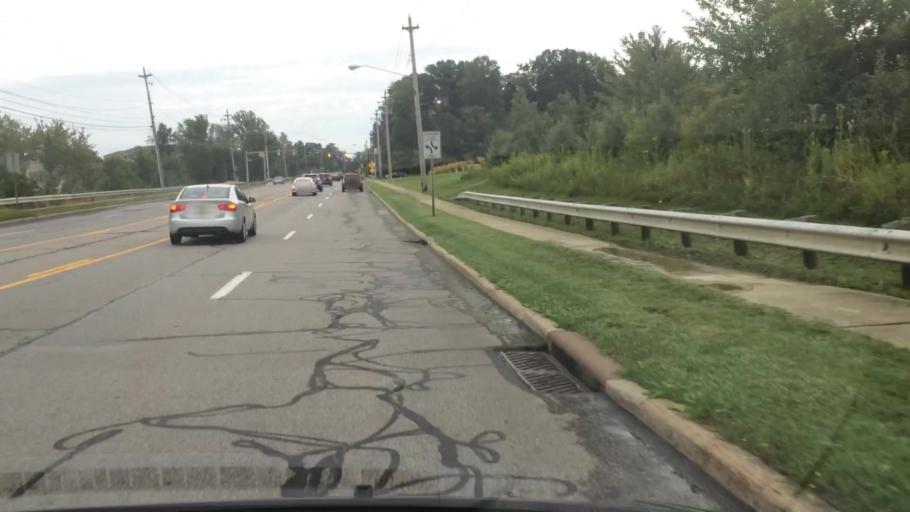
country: US
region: Ohio
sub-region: Cuyahoga County
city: Strongsville
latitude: 41.3092
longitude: -81.8146
